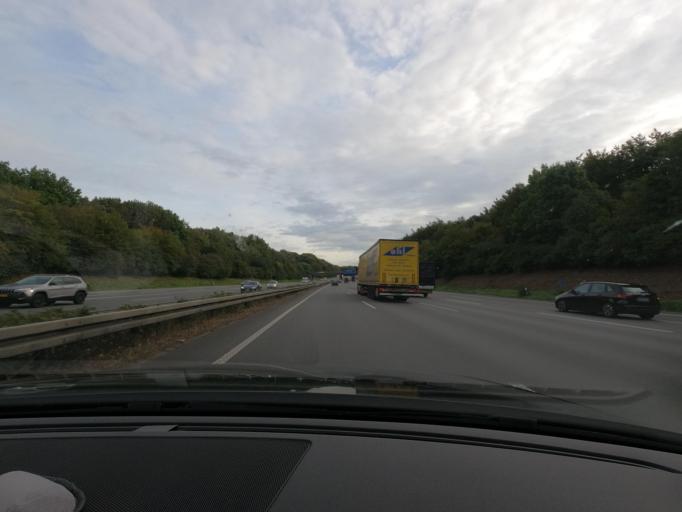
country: DE
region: North Rhine-Westphalia
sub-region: Regierungsbezirk Dusseldorf
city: Dinslaken
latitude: 51.5347
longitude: 6.8164
